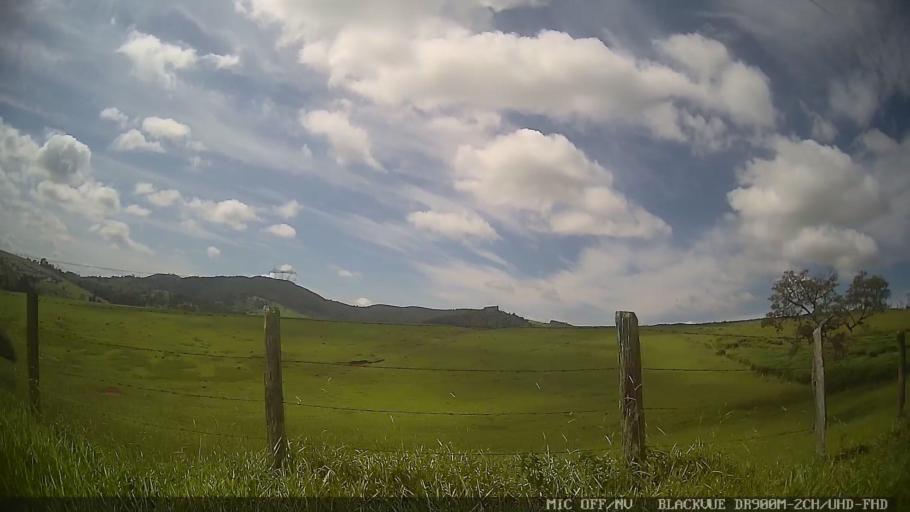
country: BR
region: Sao Paulo
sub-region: Braganca Paulista
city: Braganca Paulista
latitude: -22.9573
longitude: -46.6222
